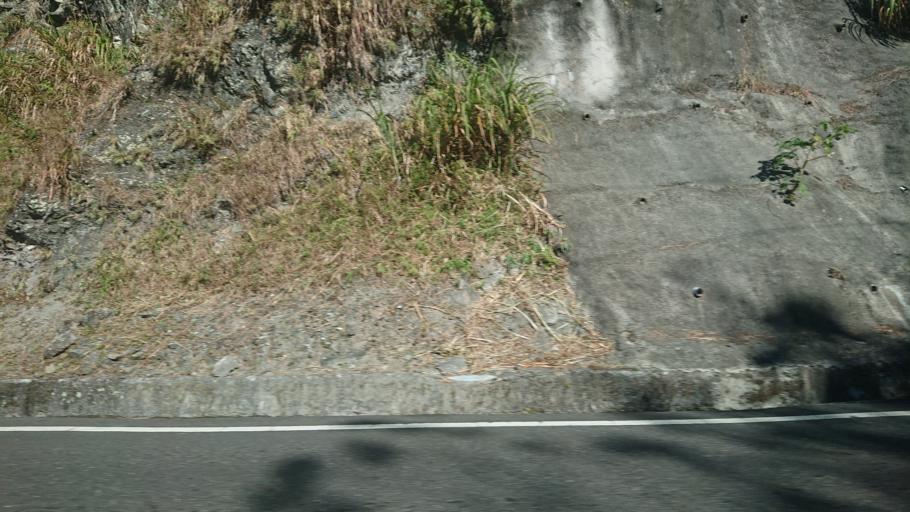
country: TW
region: Taiwan
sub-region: Chiayi
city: Jiayi Shi
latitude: 23.4632
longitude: 120.7279
